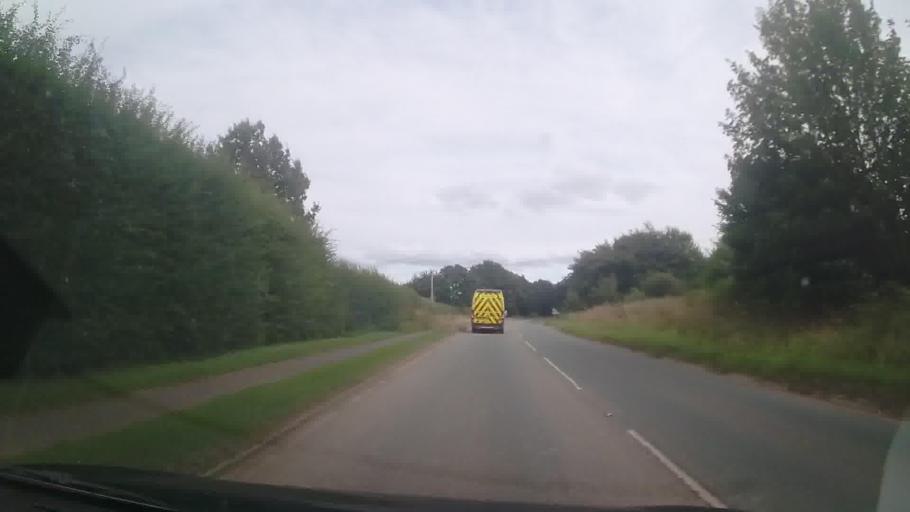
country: GB
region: England
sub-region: Shropshire
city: Bicton
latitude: 52.7194
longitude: -2.7963
